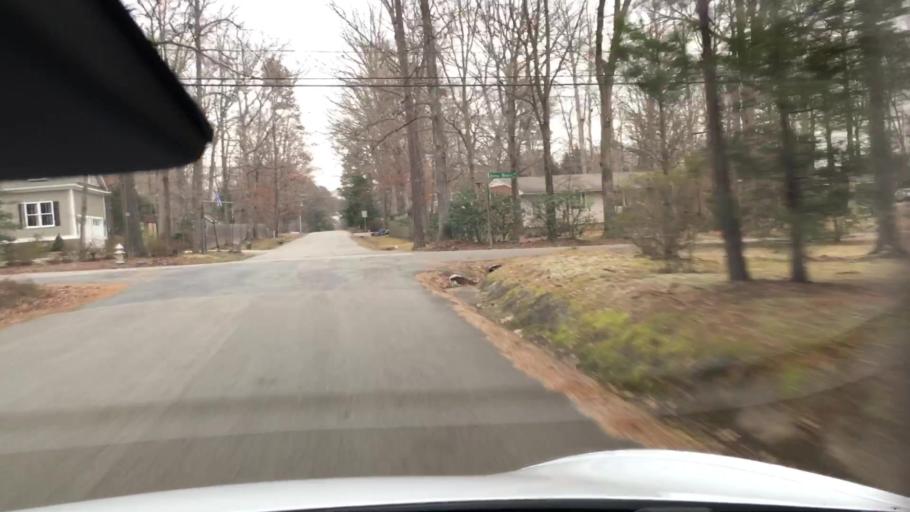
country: US
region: Virginia
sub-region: Chesterfield County
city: Bon Air
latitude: 37.5304
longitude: -77.5673
